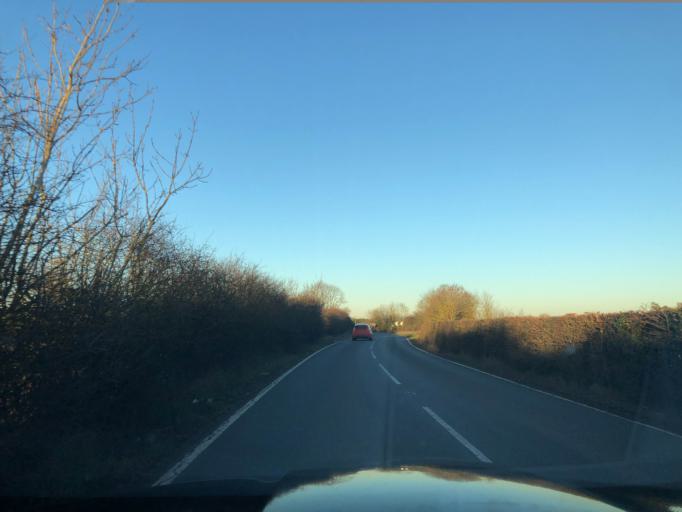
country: GB
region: England
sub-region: Warwickshire
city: Harbury
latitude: 52.1960
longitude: -1.4544
